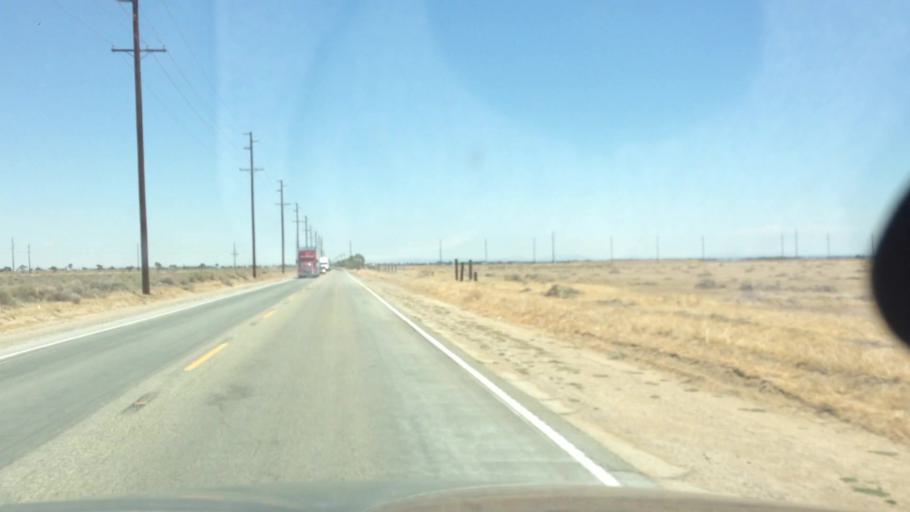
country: US
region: California
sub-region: Los Angeles County
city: Leona Valley
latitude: 34.7760
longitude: -118.3330
